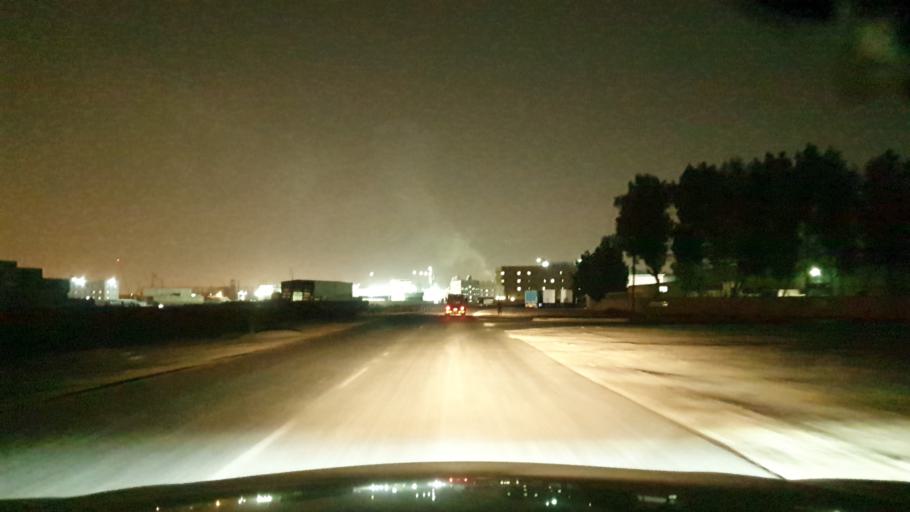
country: BH
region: Northern
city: Sitrah
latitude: 26.0924
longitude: 50.6153
